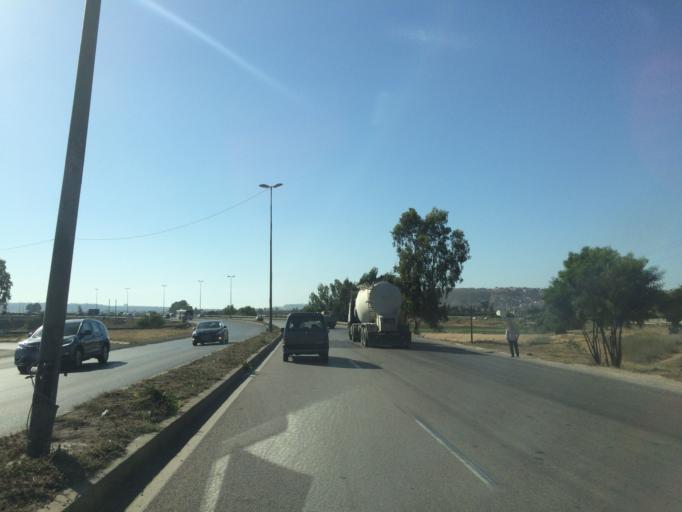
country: MA
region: Rabat-Sale-Zemmour-Zaer
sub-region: Rabat
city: Rabat
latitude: 33.9875
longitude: -6.7627
